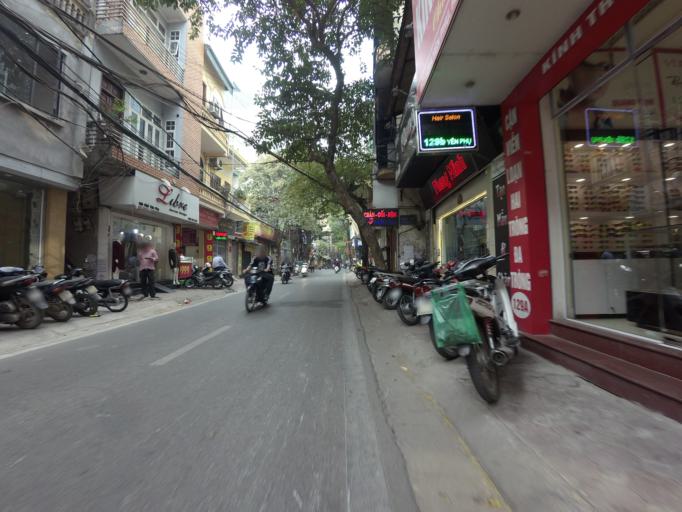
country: VN
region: Ha Noi
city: Hoan Kiem
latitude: 21.0534
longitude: 105.8363
